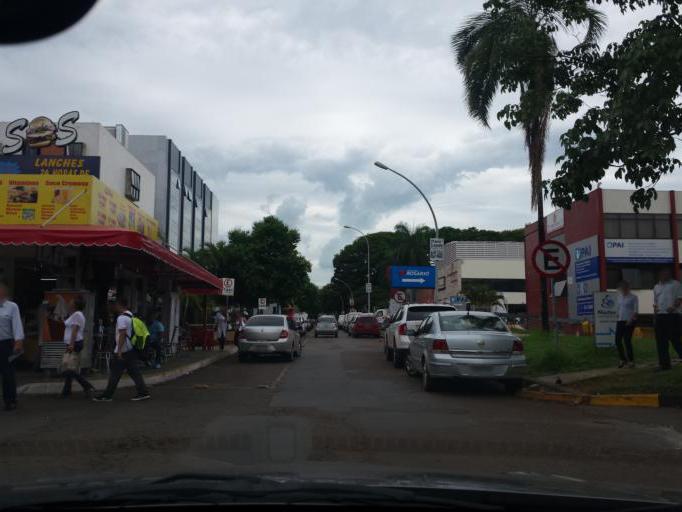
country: BR
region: Federal District
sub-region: Brasilia
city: Brasilia
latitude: -15.8283
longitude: -47.9288
